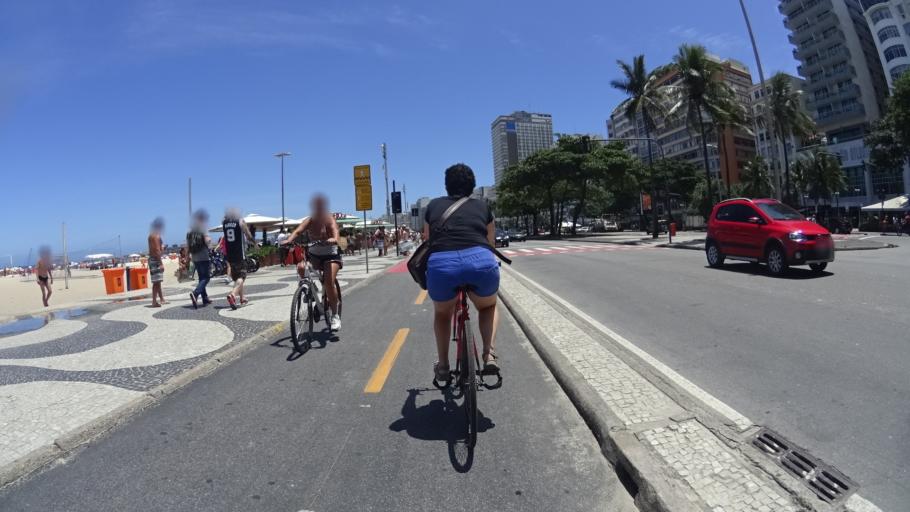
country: BR
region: Rio de Janeiro
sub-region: Rio De Janeiro
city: Rio de Janeiro
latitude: -22.9750
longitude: -43.1870
